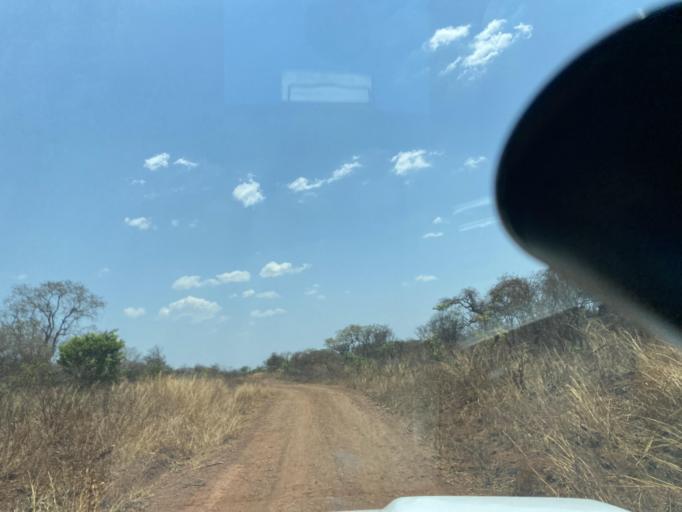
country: ZM
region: Lusaka
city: Lusaka
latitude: -15.5085
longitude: 28.0016
